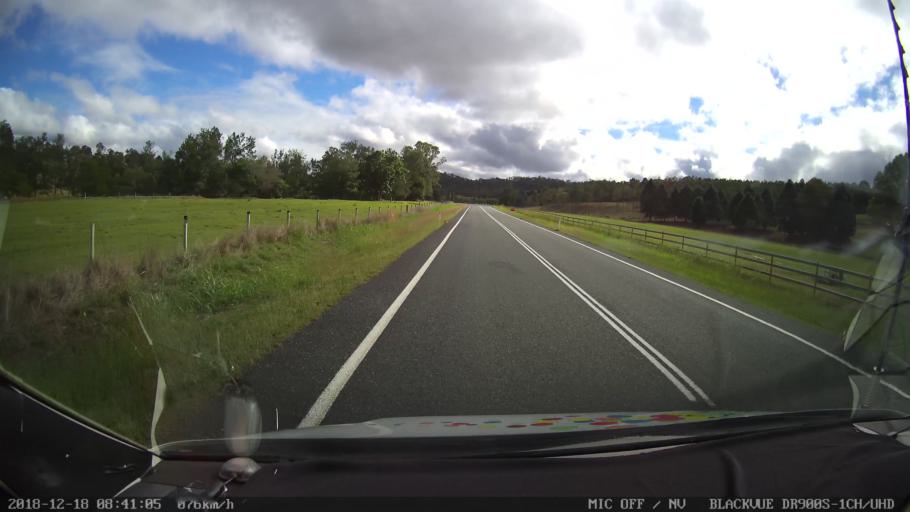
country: AU
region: Queensland
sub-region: Logan
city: Cedar Vale
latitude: -28.2394
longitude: 152.8540
